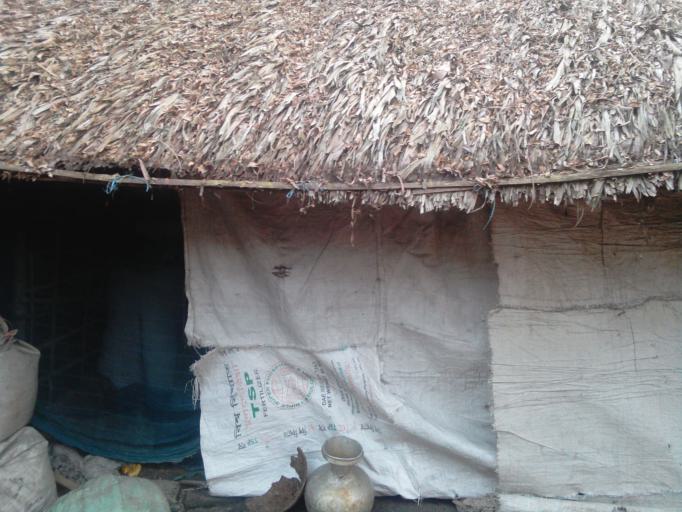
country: BD
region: Khulna
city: Kesabpur
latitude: 22.7747
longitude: 89.2282
